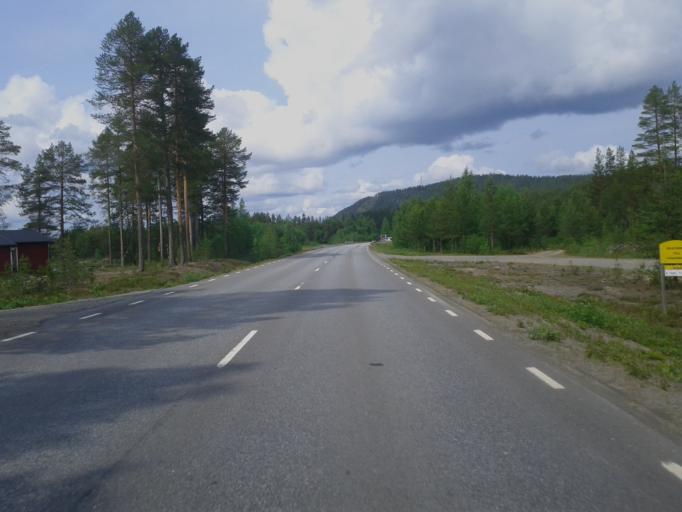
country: SE
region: Vaesterbotten
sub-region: Mala Kommun
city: Mala
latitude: 65.1596
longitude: 18.7845
